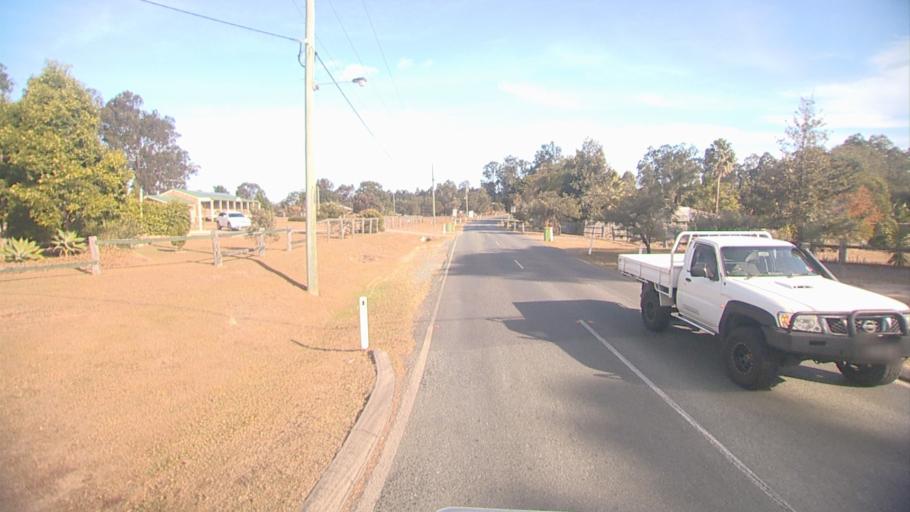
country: AU
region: Queensland
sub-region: Logan
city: Cedar Vale
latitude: -27.8652
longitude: 153.0059
